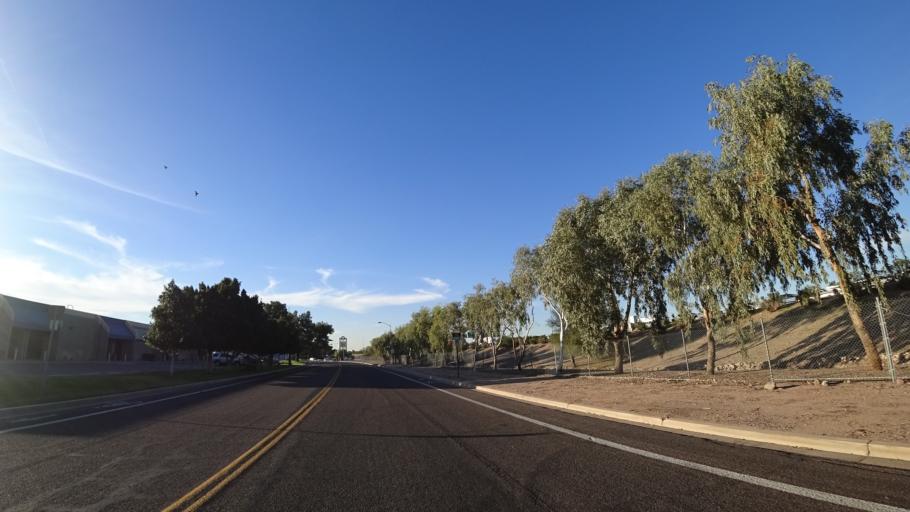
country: US
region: Arizona
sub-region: Maricopa County
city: Phoenix
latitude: 33.4231
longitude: -112.0234
